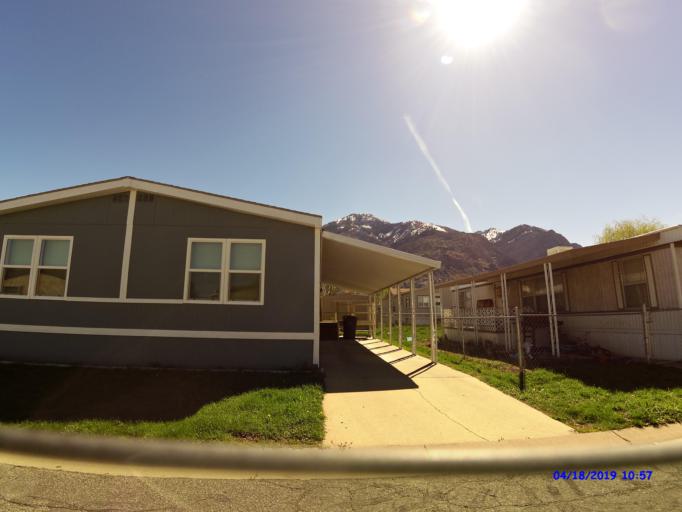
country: US
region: Utah
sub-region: Weber County
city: Harrisville
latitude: 41.2842
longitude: -111.9655
